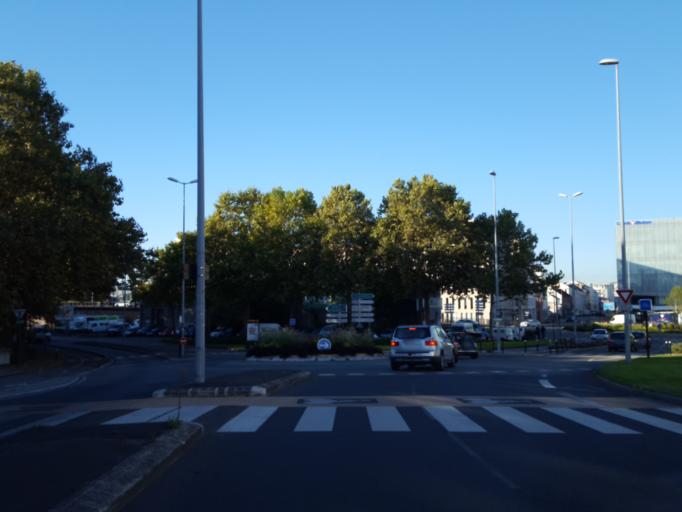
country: FR
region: Pays de la Loire
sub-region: Departement de la Loire-Atlantique
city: Nantes
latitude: 47.2124
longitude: -1.5421
